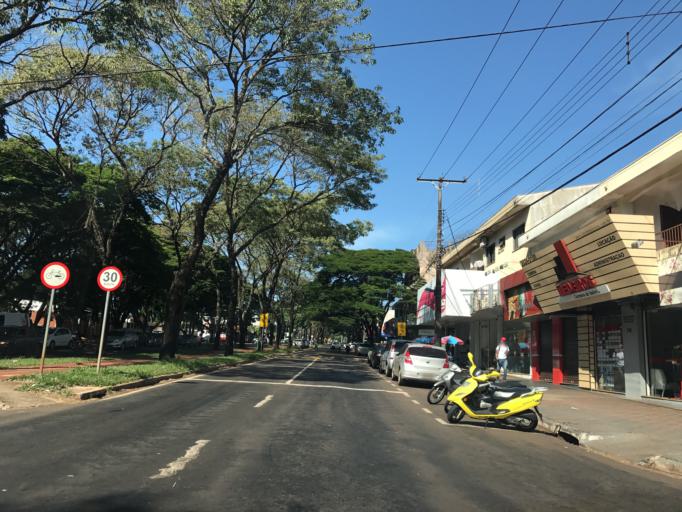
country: BR
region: Parana
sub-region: Maringa
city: Maringa
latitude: -23.4091
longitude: -51.9560
